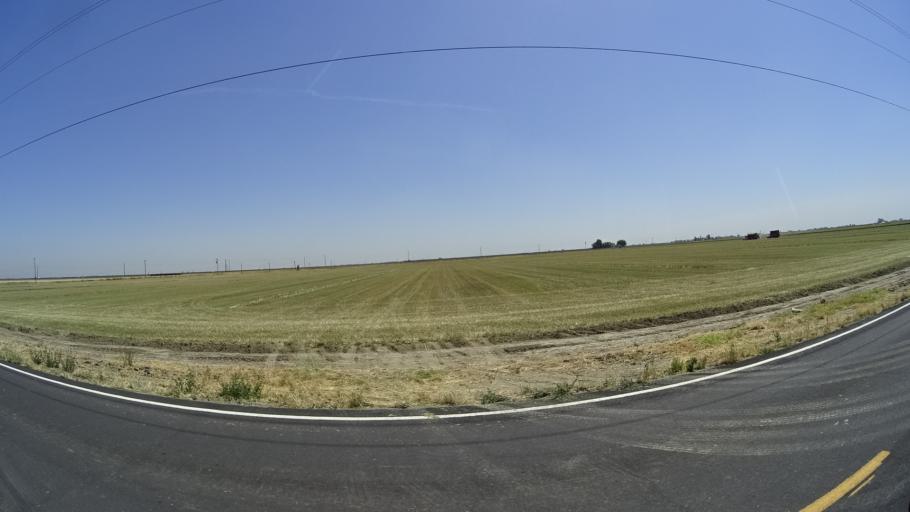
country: US
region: California
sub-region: Kings County
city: Corcoran
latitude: 36.0640
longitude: -119.5363
